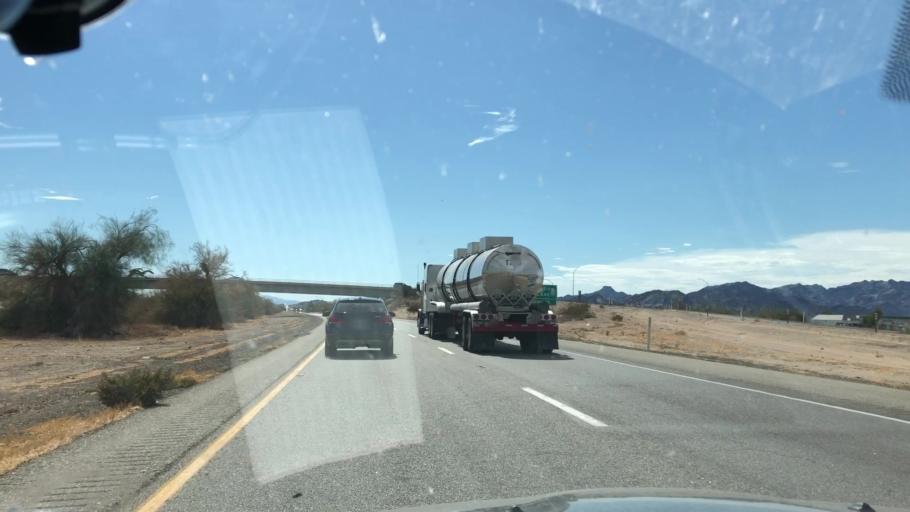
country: US
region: California
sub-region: Riverside County
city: Mesa Verde
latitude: 33.6095
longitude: -114.7249
